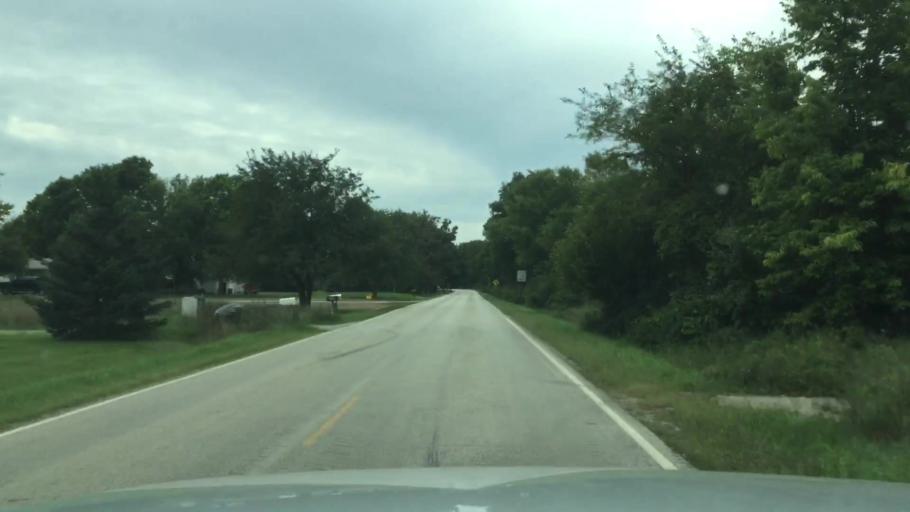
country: US
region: Michigan
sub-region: Shiawassee County
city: Durand
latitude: 42.9381
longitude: -84.0415
